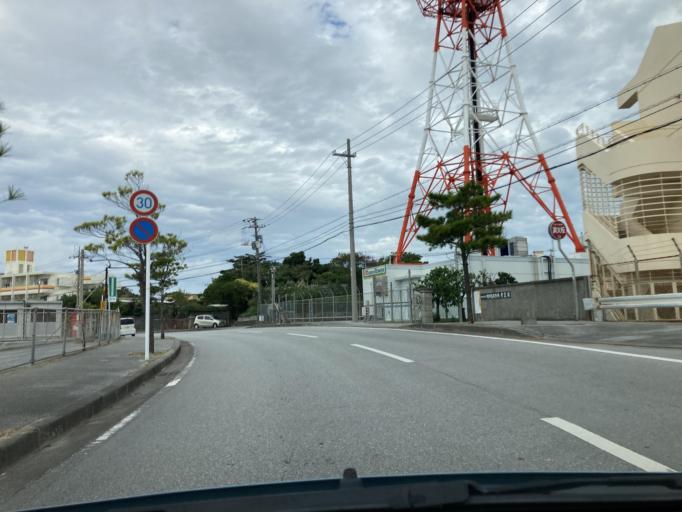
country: JP
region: Okinawa
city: Ginowan
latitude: 26.2173
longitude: 127.7341
